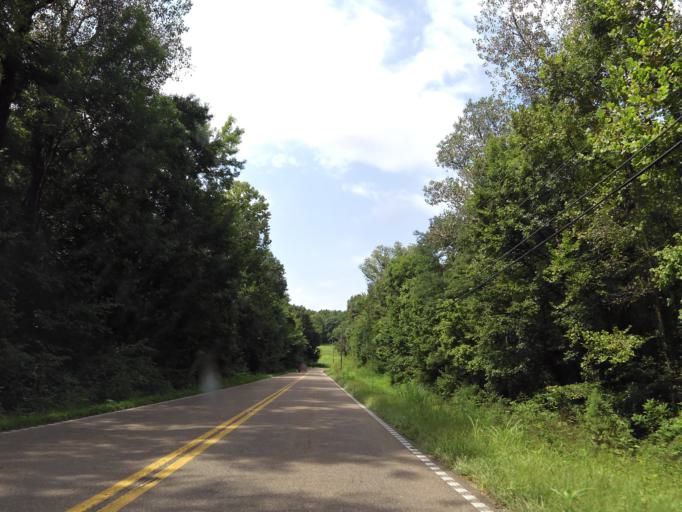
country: US
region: Tennessee
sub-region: Decatur County
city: Decaturville
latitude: 35.5813
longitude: -88.0731
